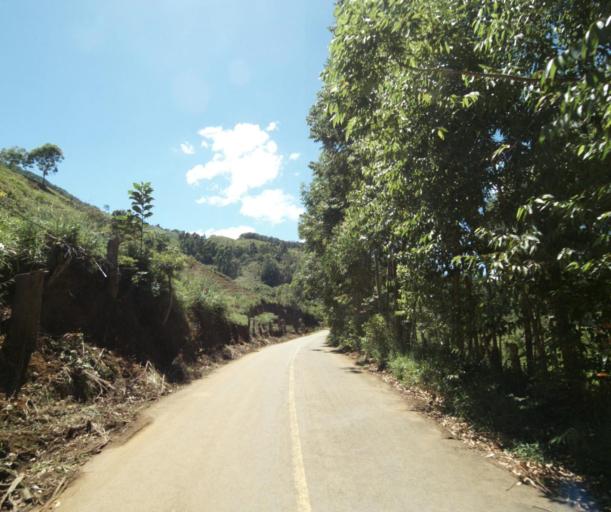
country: BR
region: Minas Gerais
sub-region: Espera Feliz
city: Espera Feliz
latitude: -20.6232
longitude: -41.8226
